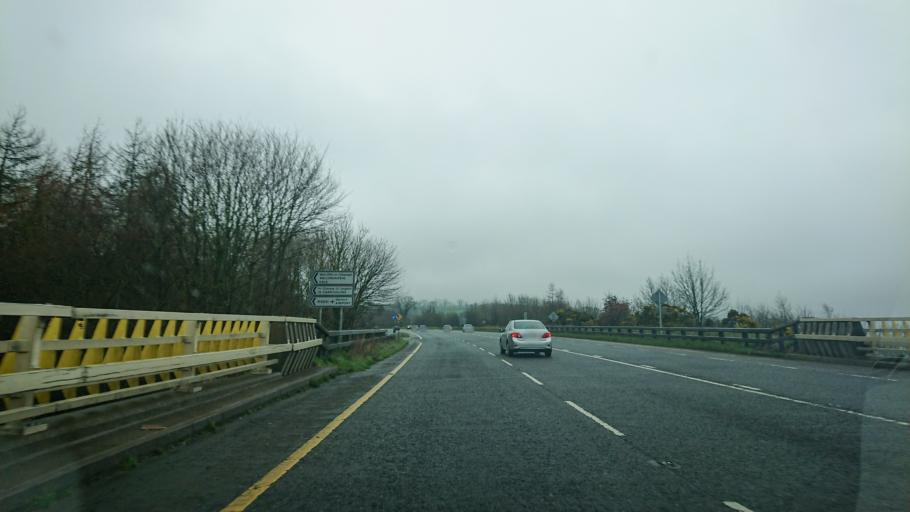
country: IE
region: Munster
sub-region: County Cork
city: Kinsale
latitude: 51.8120
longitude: -8.5382
